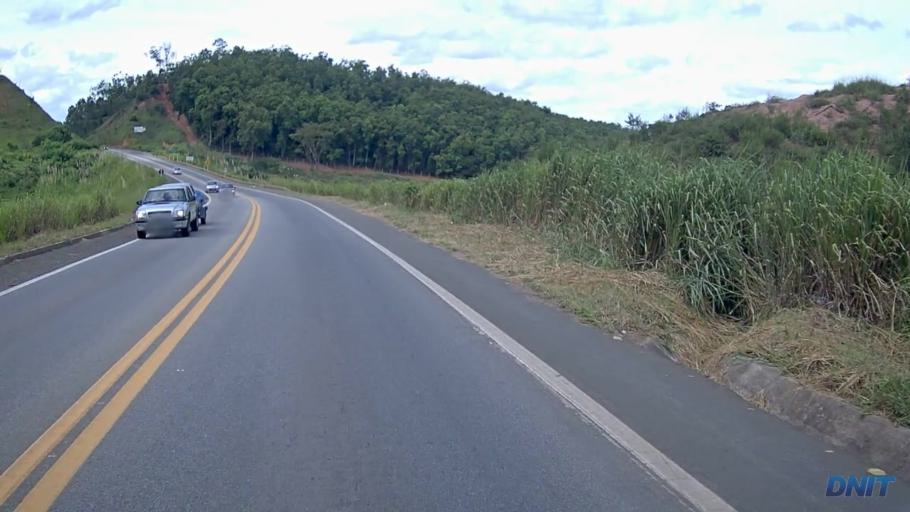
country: BR
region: Minas Gerais
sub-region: Ipatinga
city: Ipatinga
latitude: -19.4490
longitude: -42.5159
